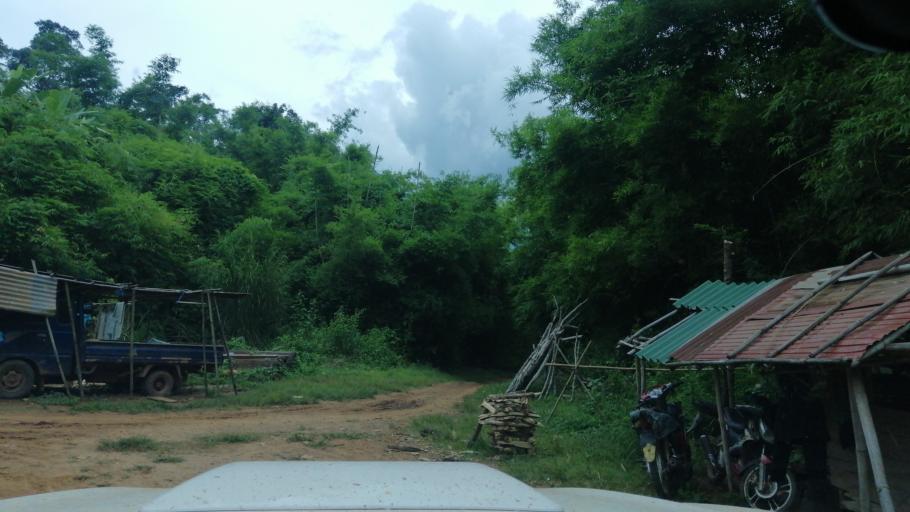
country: TH
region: Nan
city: Mae Charim
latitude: 18.7436
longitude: 101.2839
